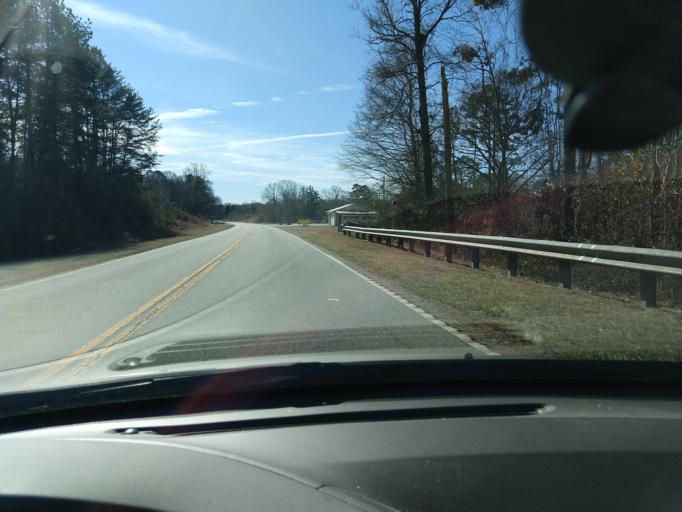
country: US
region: South Carolina
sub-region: Oconee County
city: Westminster
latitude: 34.6573
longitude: -83.1314
